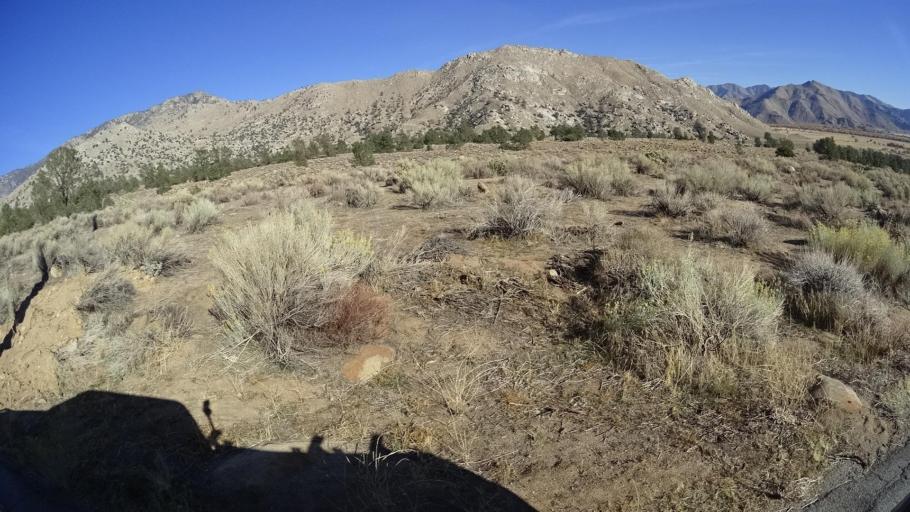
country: US
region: California
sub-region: Kern County
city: Weldon
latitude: 35.6992
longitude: -118.3023
